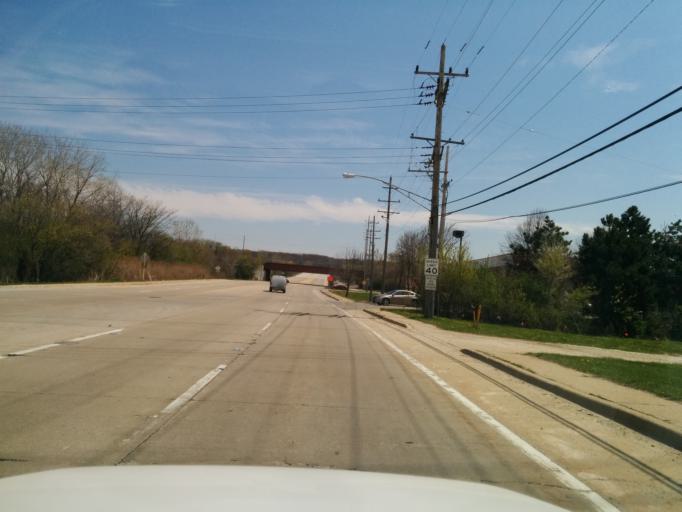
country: US
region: Illinois
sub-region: Cook County
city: Willow Springs
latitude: 41.7381
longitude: -87.8850
